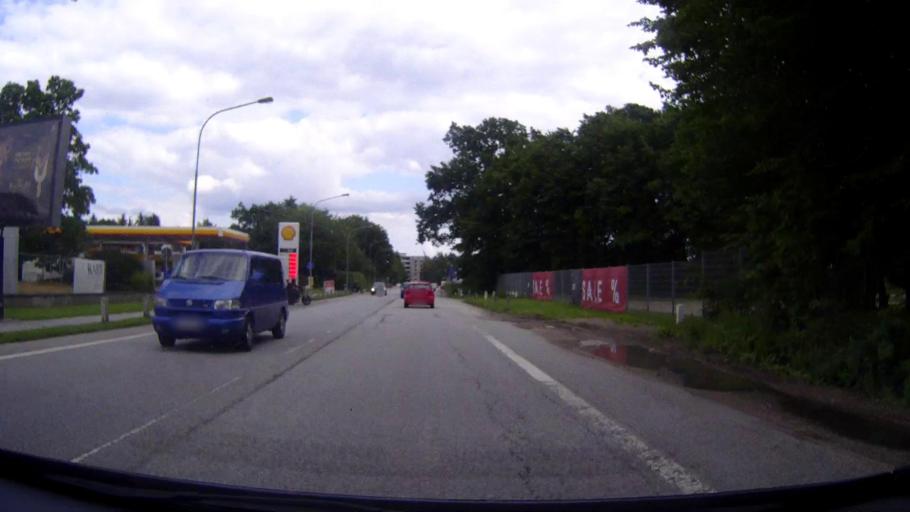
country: DE
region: Schleswig-Holstein
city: Stockelsdorf
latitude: 53.8561
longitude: 10.6354
